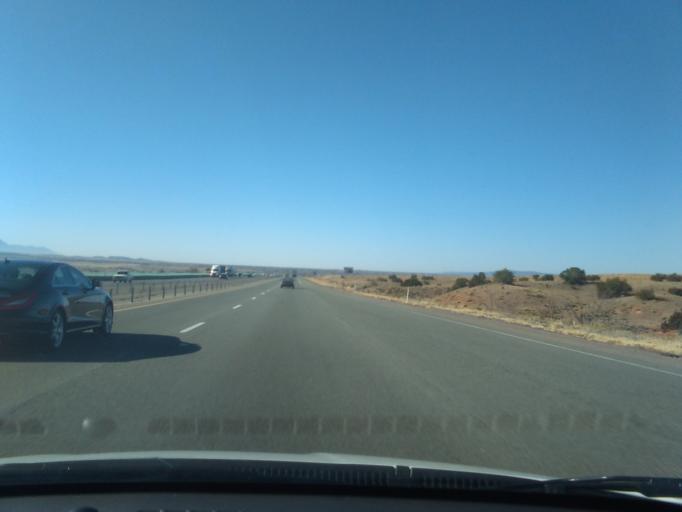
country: US
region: New Mexico
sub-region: Santa Fe County
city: La Cienega
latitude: 35.5135
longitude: -106.2313
